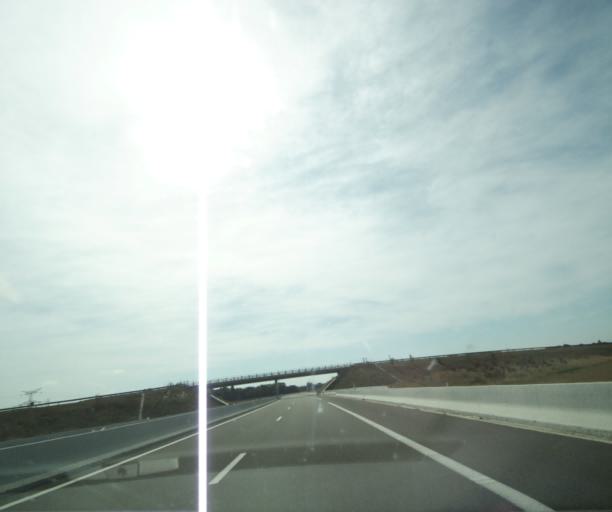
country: FR
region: Auvergne
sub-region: Departement de l'Allier
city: Vendat
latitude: 46.1290
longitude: 3.3000
